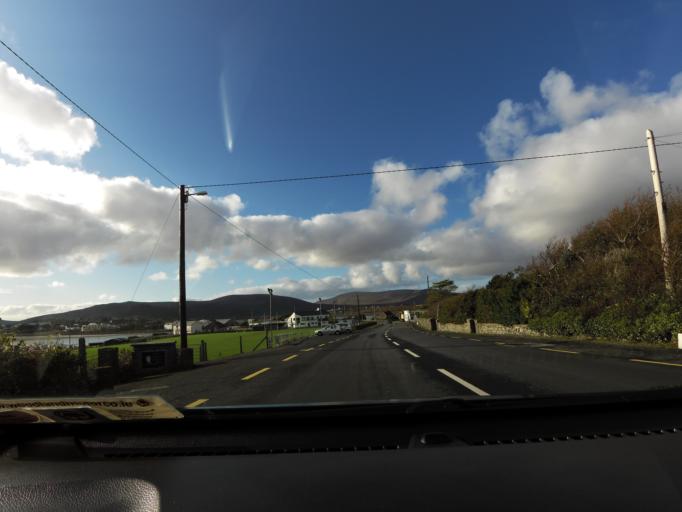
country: IE
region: Connaught
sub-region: Maigh Eo
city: Belmullet
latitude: 53.9335
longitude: -9.9150
